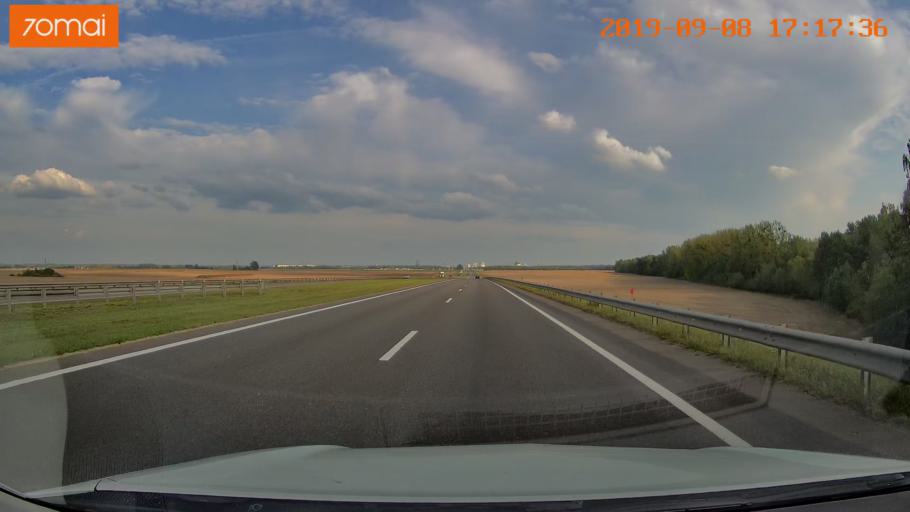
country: BY
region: Grodnenskaya
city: Skidal'
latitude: 53.5932
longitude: 24.1514
